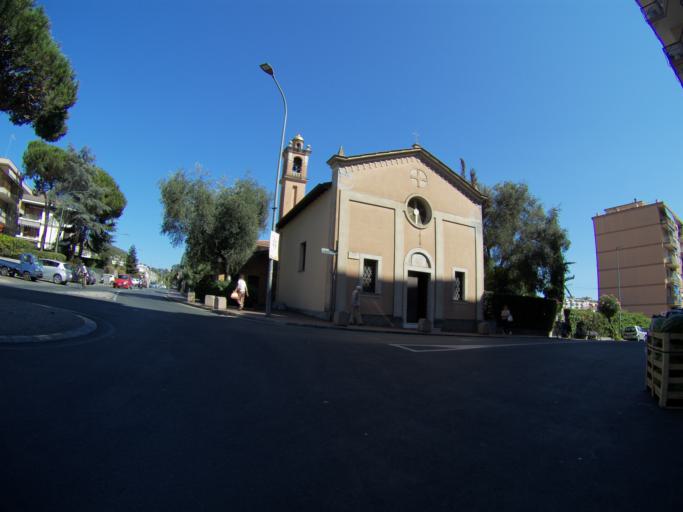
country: IT
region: Liguria
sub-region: Provincia di Imperia
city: Vallecrosia
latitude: 43.7900
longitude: 7.6376
